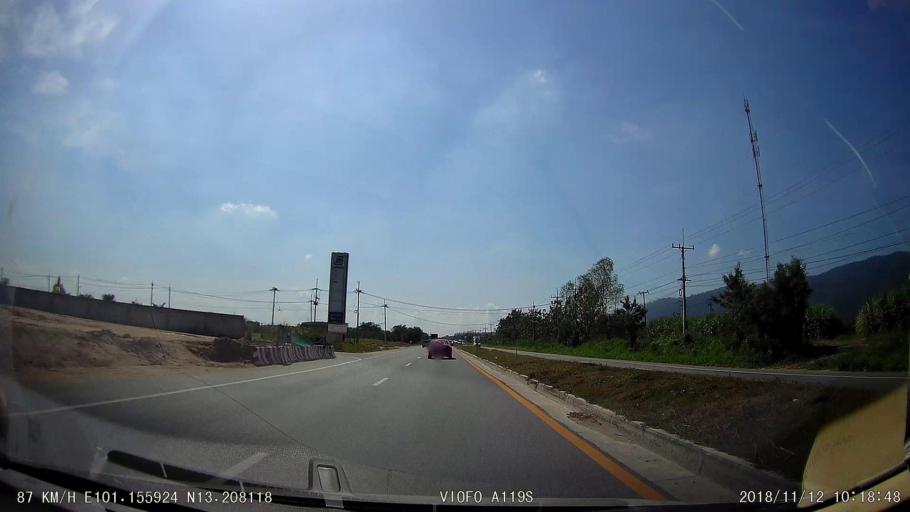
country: TH
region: Chon Buri
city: Ban Bueng
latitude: 13.2077
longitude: 101.1559
